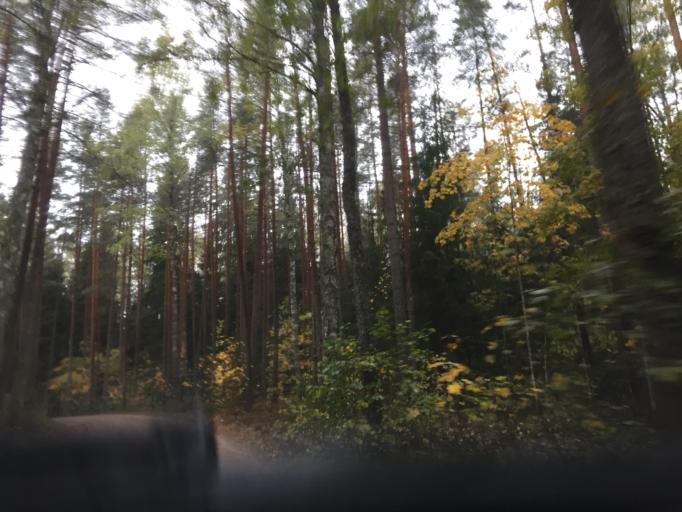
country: LV
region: Engure
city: Smarde
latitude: 56.9195
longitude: 23.4700
